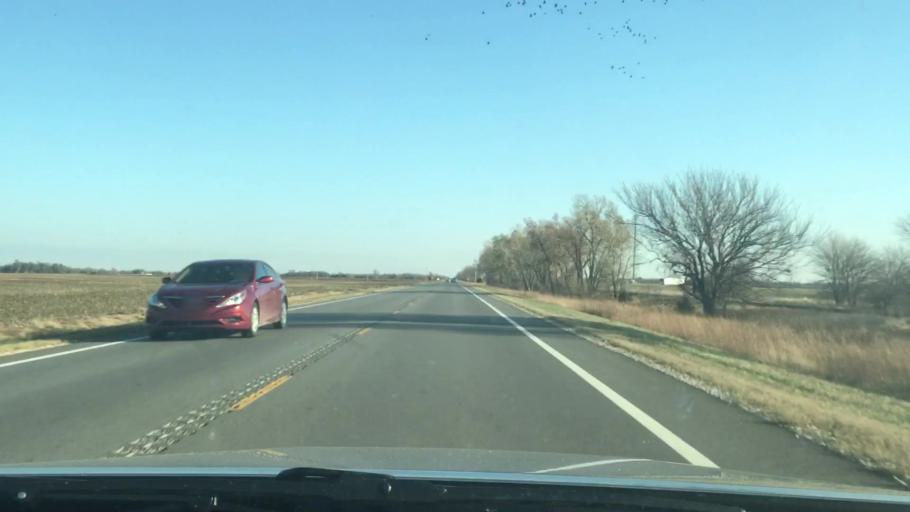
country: US
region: Kansas
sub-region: Reno County
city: Nickerson
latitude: 38.1337
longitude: -98.0638
